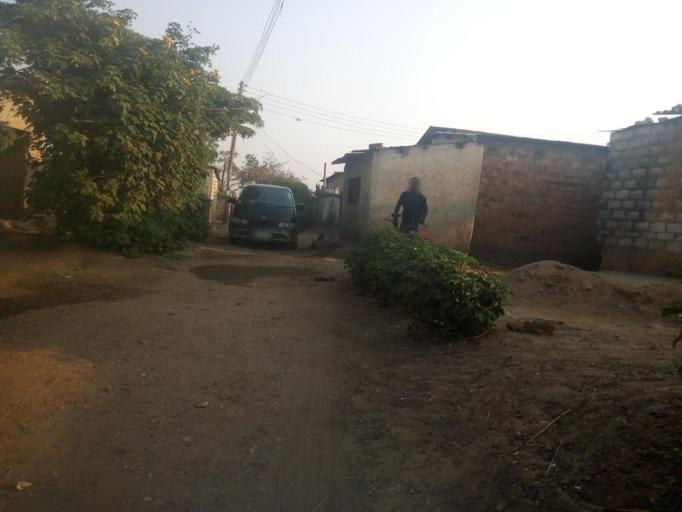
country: ZM
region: Lusaka
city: Lusaka
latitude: -15.4100
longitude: 28.3634
